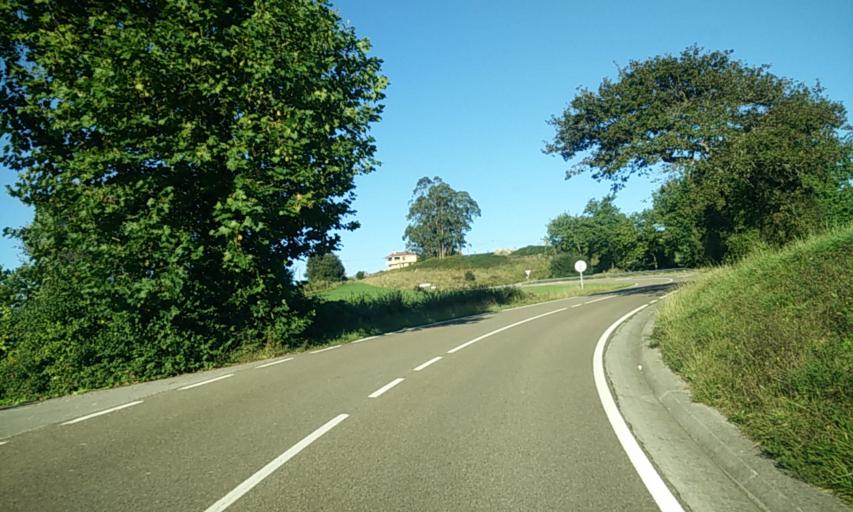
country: ES
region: Cantabria
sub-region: Provincia de Cantabria
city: San Vicente de la Barquera
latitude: 43.3818
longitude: -4.3521
